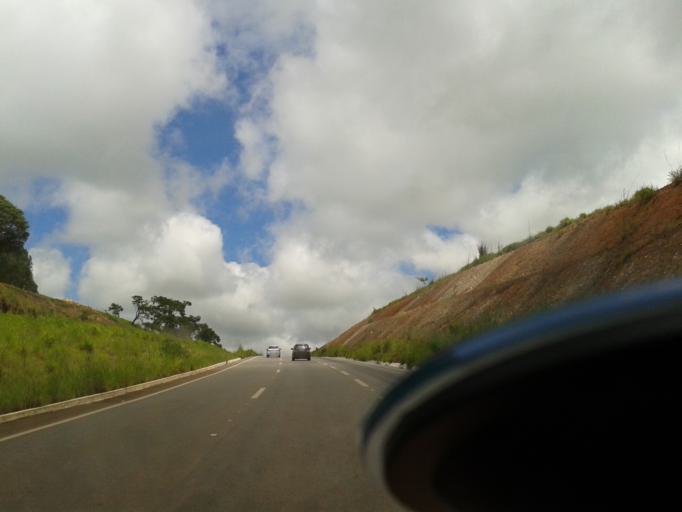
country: BR
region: Goias
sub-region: Itaberai
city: Itaberai
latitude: -16.1584
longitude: -49.6250
